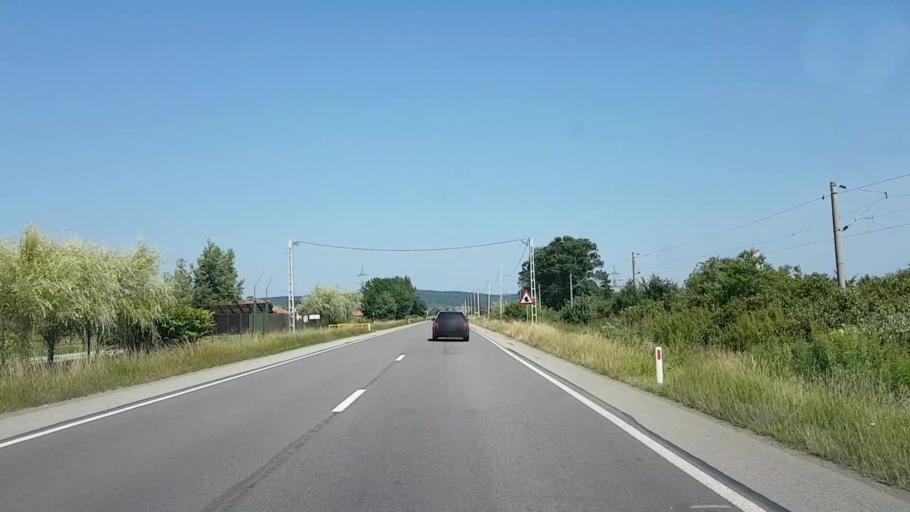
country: RO
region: Bistrita-Nasaud
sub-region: Comuna Sintereag
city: Cociu
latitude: 47.1814
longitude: 24.2564
